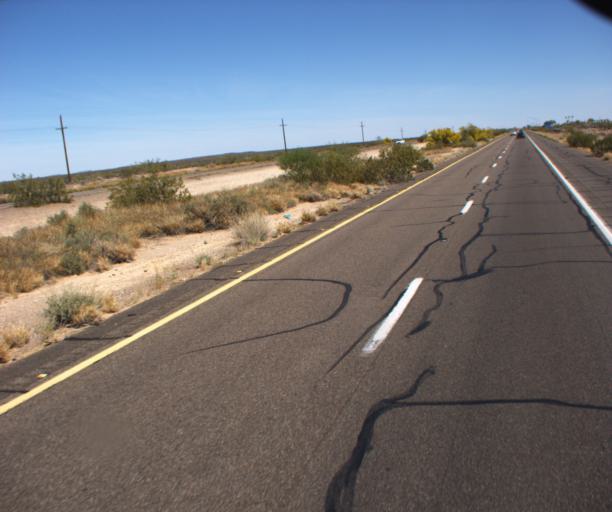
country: US
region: Arizona
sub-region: Maricopa County
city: Gila Bend
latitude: 32.8470
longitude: -113.2742
